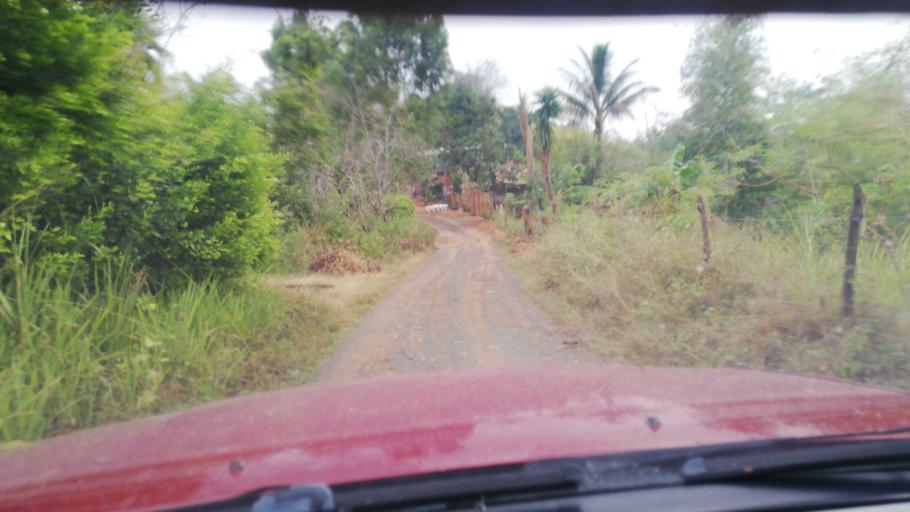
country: CO
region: Risaralda
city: Balboa
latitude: 4.8882
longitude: -75.9600
